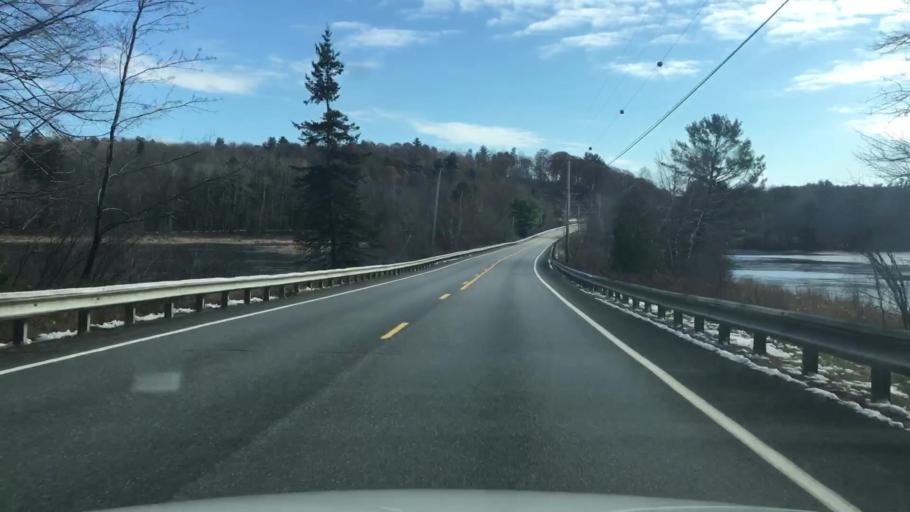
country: US
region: Maine
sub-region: Kennebec County
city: Wayne
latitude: 44.3393
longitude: -70.0204
